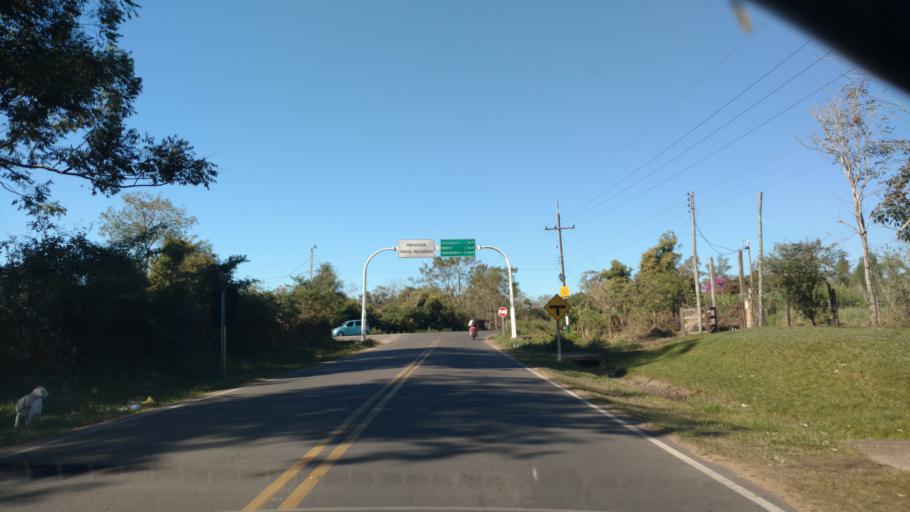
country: PY
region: Central
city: Ypacarai
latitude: -25.4397
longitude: -57.2778
